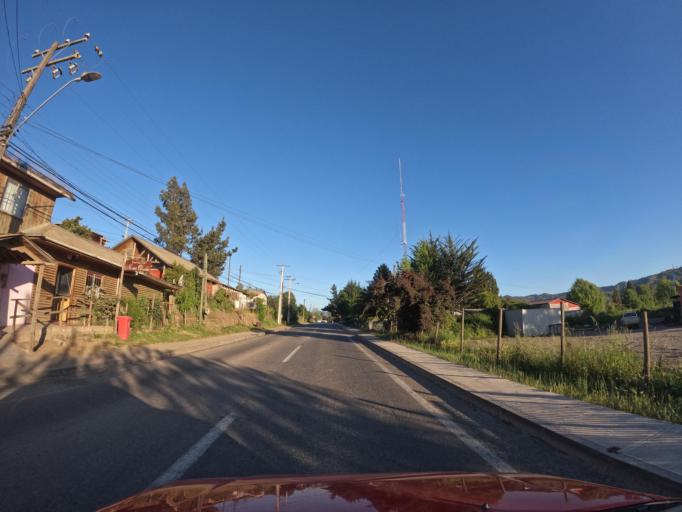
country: CL
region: Maule
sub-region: Provincia de Talca
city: Talca
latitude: -34.9925
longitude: -71.9777
